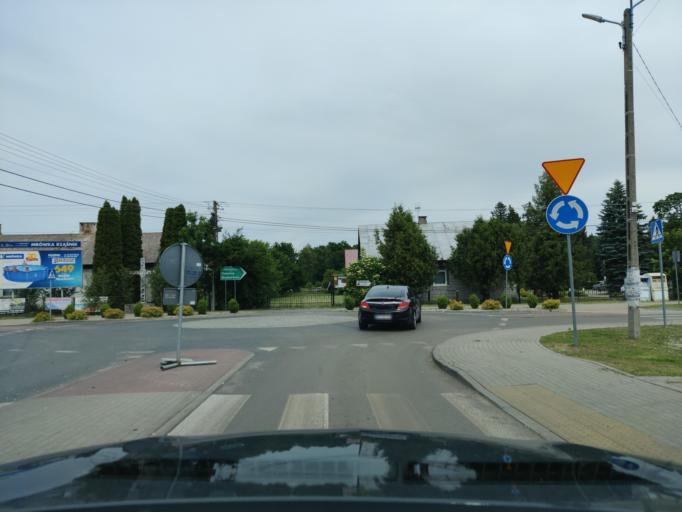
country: PL
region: Masovian Voivodeship
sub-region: Powiat wyszkowski
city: Rzasnik
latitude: 52.6986
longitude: 21.4237
